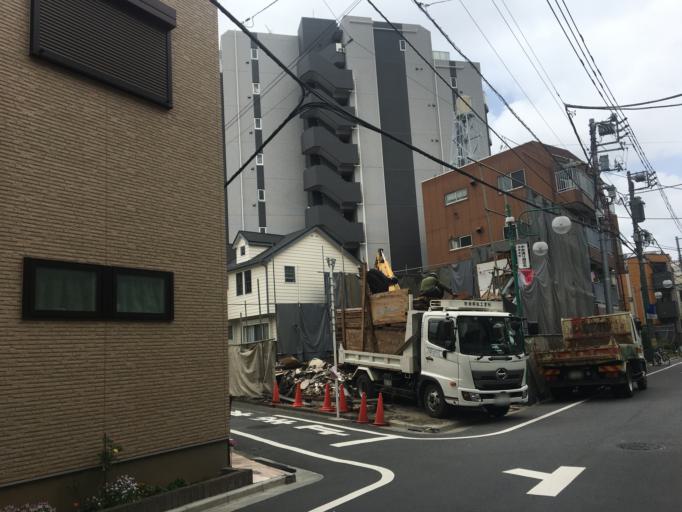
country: JP
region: Tokyo
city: Tokyo
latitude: 35.7424
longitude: 139.7117
